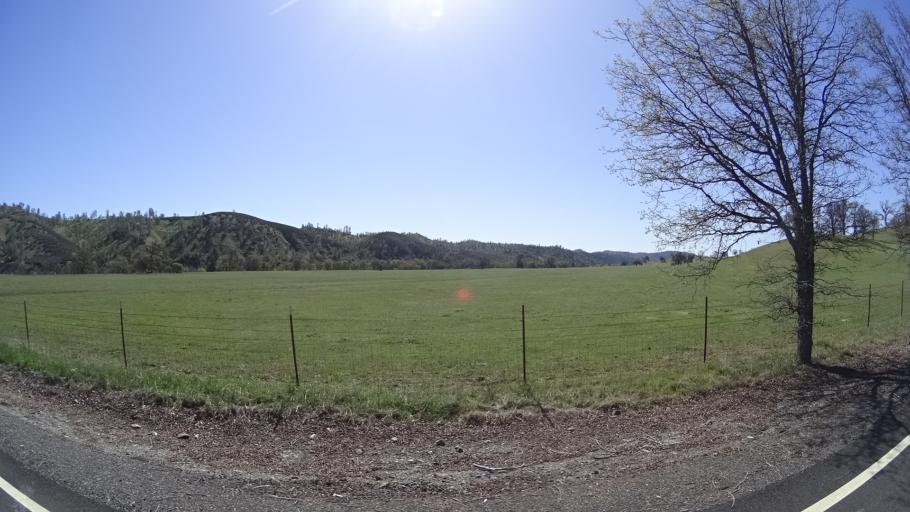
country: US
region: California
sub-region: Glenn County
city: Orland
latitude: 39.6617
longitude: -122.5292
